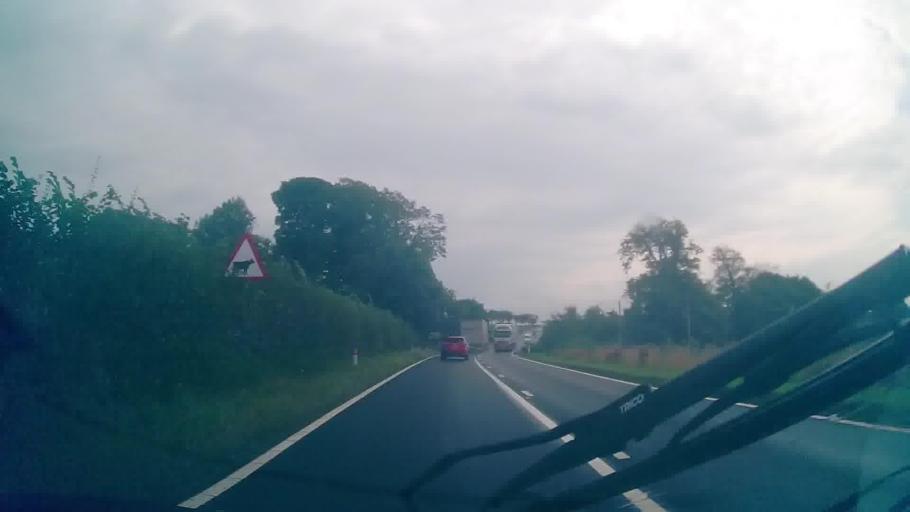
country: GB
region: Scotland
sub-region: Dumfries and Galloway
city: Lochmaben
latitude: 55.0529
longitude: -3.4648
